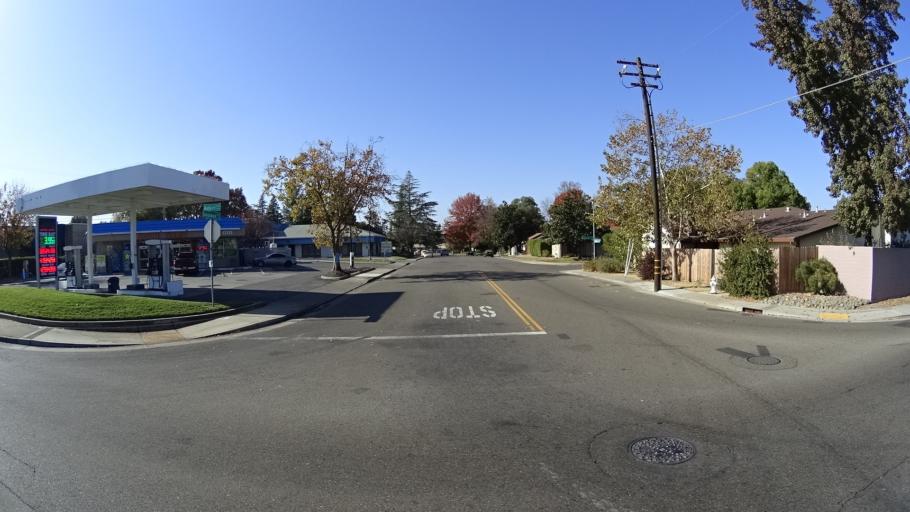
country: US
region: California
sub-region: Sacramento County
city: Citrus Heights
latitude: 38.7161
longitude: -121.2905
